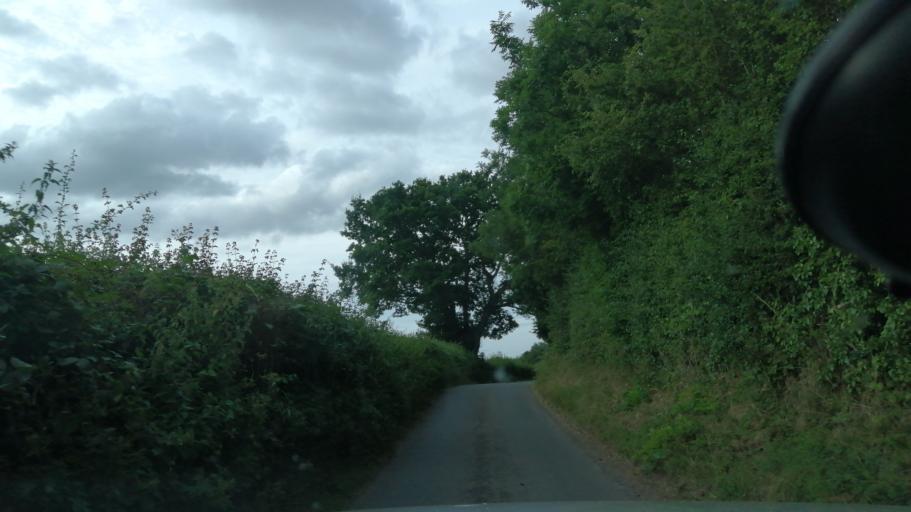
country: GB
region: England
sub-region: Herefordshire
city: Thruxton
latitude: 52.0110
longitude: -2.8031
